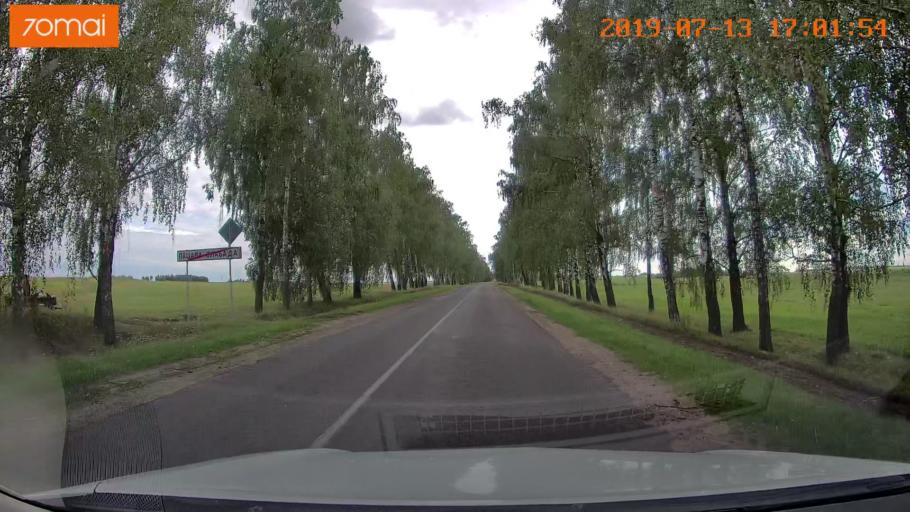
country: BY
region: Mogilev
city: Kirawsk
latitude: 53.2913
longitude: 29.3921
